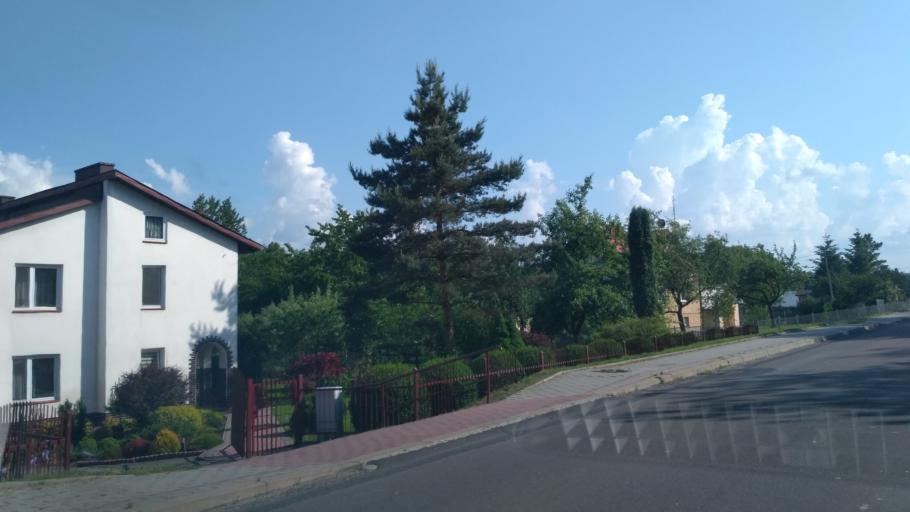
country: PL
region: Subcarpathian Voivodeship
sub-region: Powiat jaroslawski
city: Pruchnik
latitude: 49.8988
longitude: 22.5034
